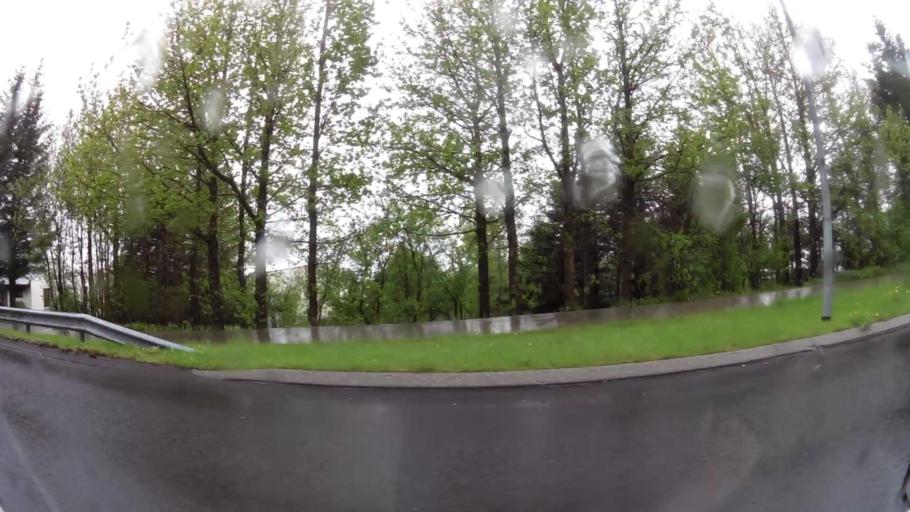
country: IS
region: Capital Region
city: Reykjavik
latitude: 64.1019
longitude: -21.8421
